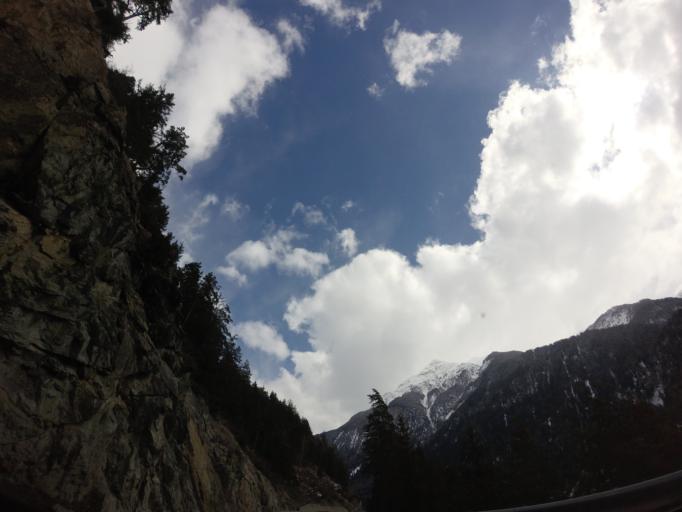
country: CH
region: Grisons
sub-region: Inn District
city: Scuol
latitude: 46.8343
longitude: 10.3999
